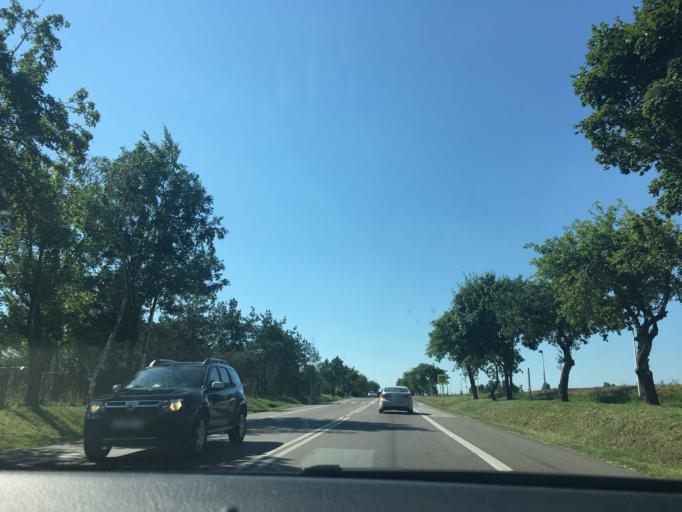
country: PL
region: Lublin Voivodeship
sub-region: Powiat lubelski
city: Niemce
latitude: 51.3533
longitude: 22.6205
